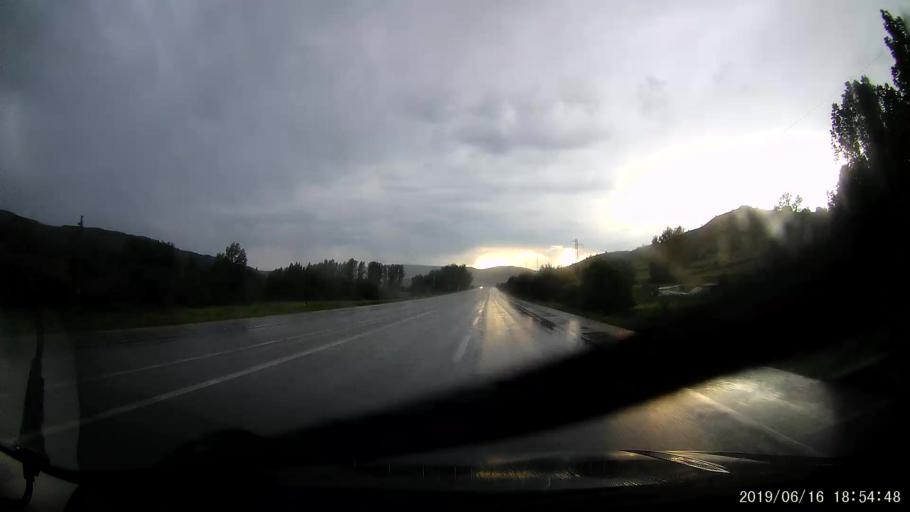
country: TR
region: Erzincan
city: Catalcam
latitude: 39.8979
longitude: 38.8445
